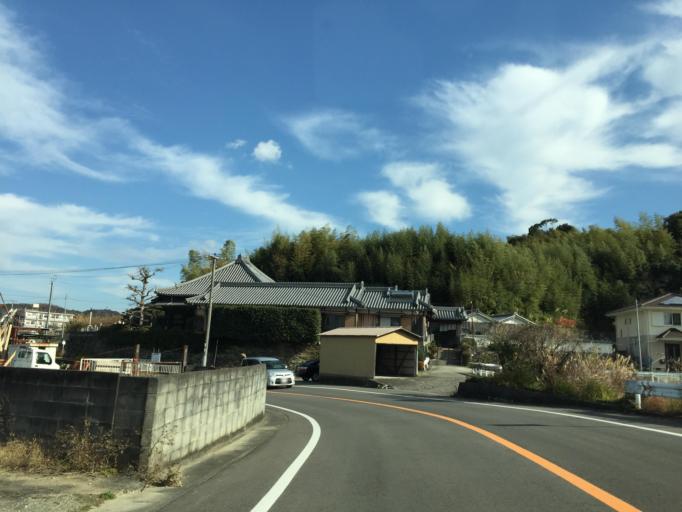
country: JP
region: Wakayama
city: Kainan
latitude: 34.1713
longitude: 135.2250
